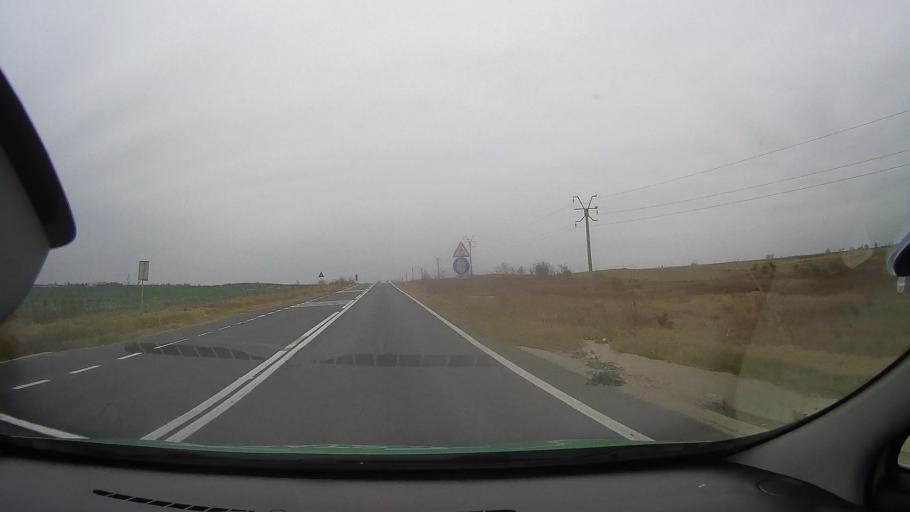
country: RO
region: Constanta
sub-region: Oras Harsova
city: Harsova
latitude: 44.6926
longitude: 27.9389
